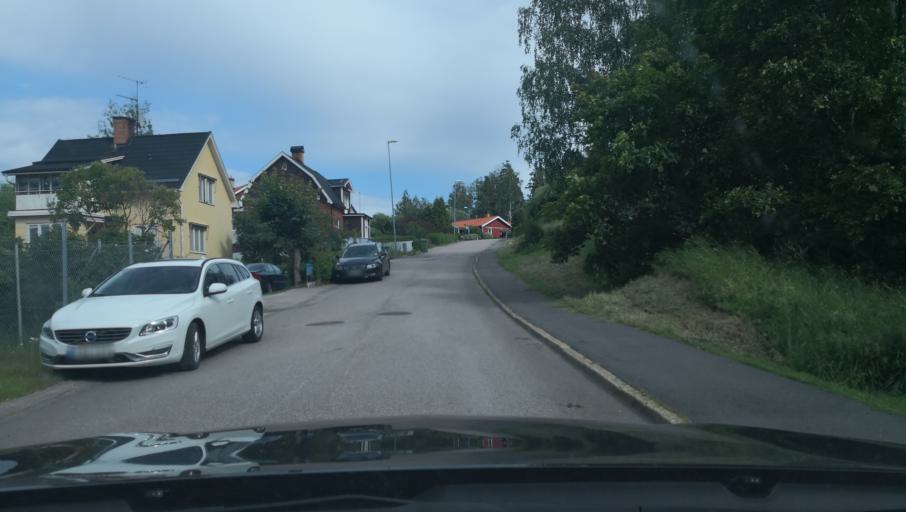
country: SE
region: Vaestmanland
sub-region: Fagersta Kommun
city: Fagersta
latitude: 59.9891
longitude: 15.8273
